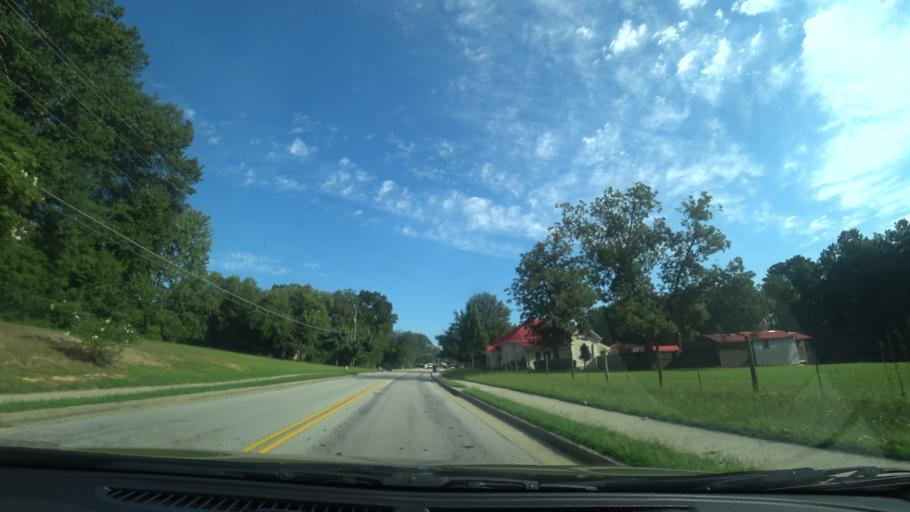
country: US
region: Georgia
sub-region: Gwinnett County
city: Grayson
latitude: 33.8890
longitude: -83.9605
